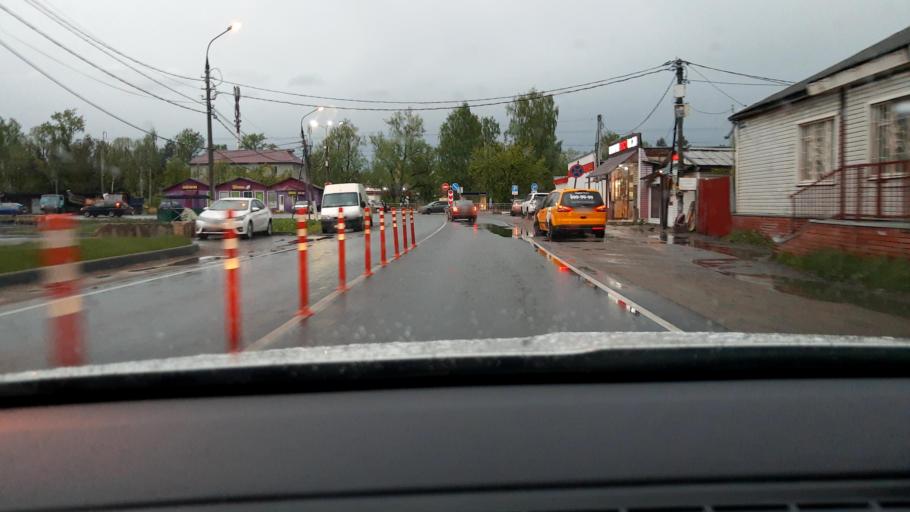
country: RU
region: Moskovskaya
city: Zagoryanskiy
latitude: 55.9253
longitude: 37.9141
